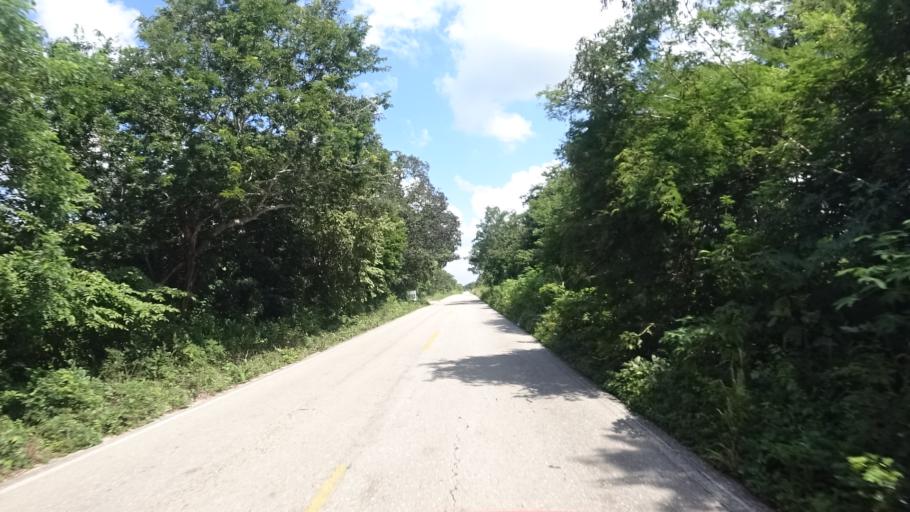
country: MX
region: Yucatan
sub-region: Panaba
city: Loche
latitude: 21.4114
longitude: -88.1427
